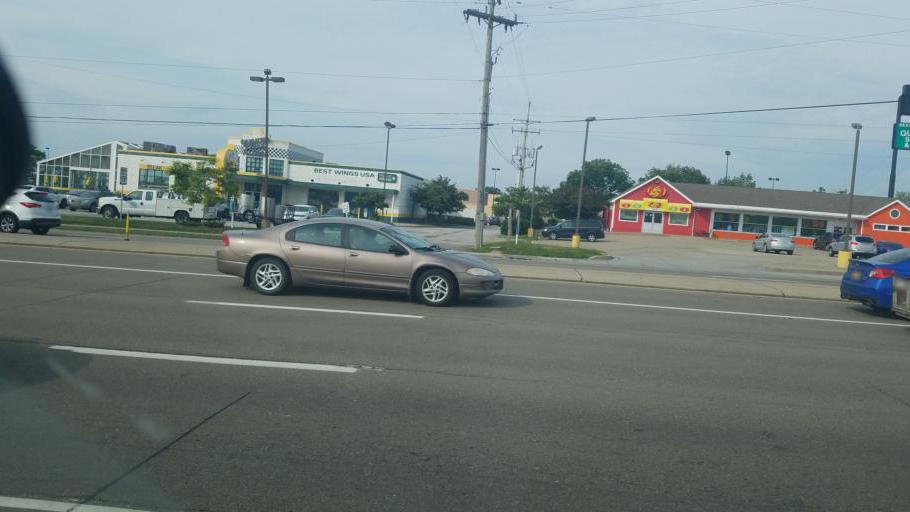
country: US
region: Pennsylvania
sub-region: Erie County
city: Erie
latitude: 42.0503
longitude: -80.0828
